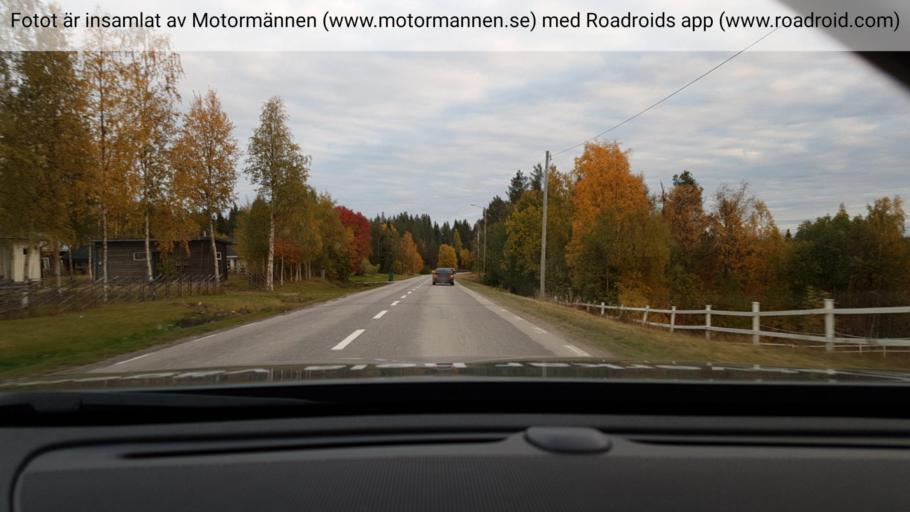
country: SE
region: Norrbotten
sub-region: Jokkmokks Kommun
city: Jokkmokk
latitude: 66.1524
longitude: 19.9835
